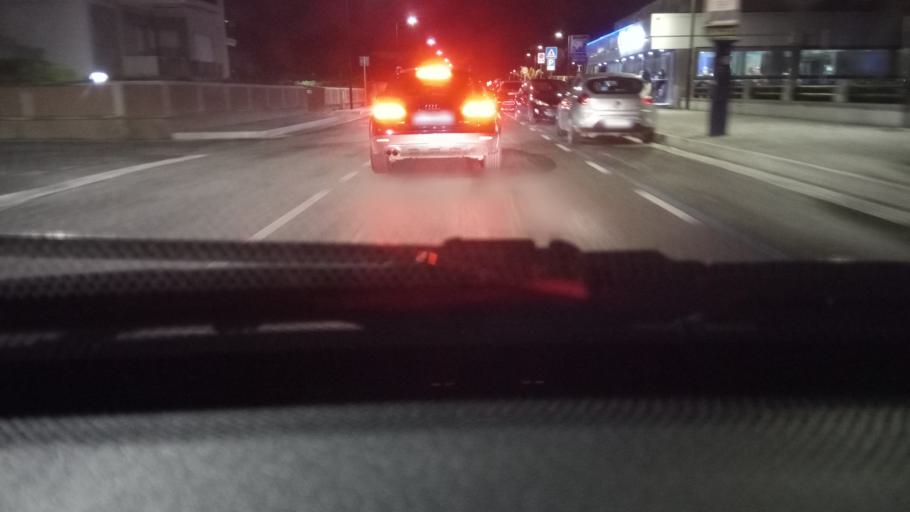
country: IT
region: Latium
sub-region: Provincia di Latina
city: Minturno
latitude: 41.2503
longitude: 13.7172
